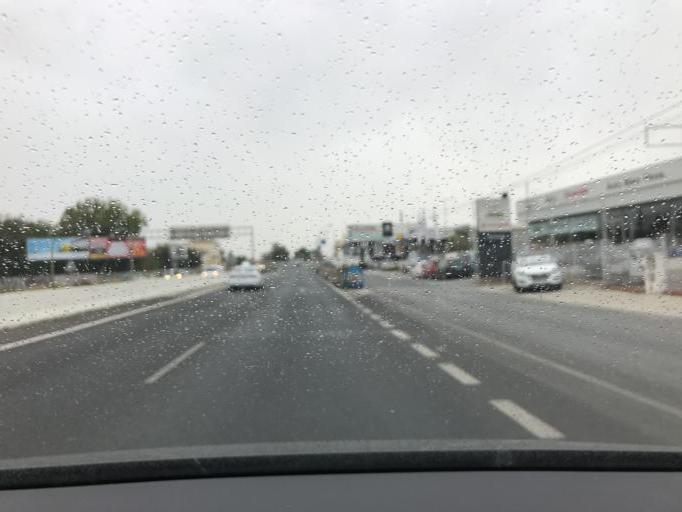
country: ES
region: Andalusia
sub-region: Provincia de Granada
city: Atarfe
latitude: 37.1927
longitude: -3.7190
